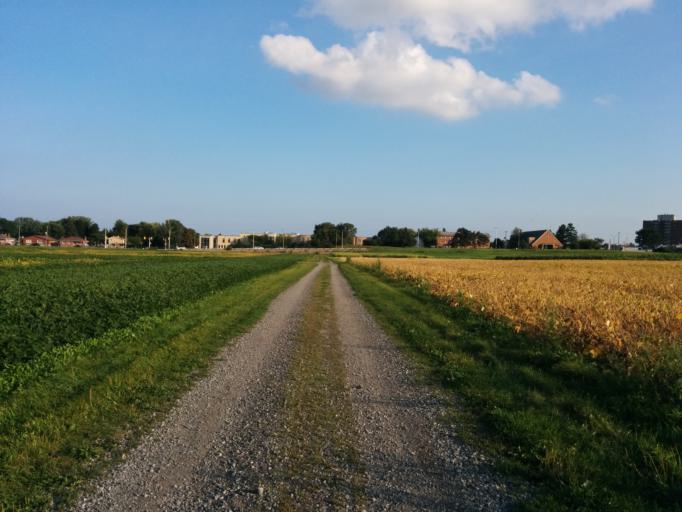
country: CA
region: Ontario
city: Ottawa
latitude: 45.3690
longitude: -75.7301
